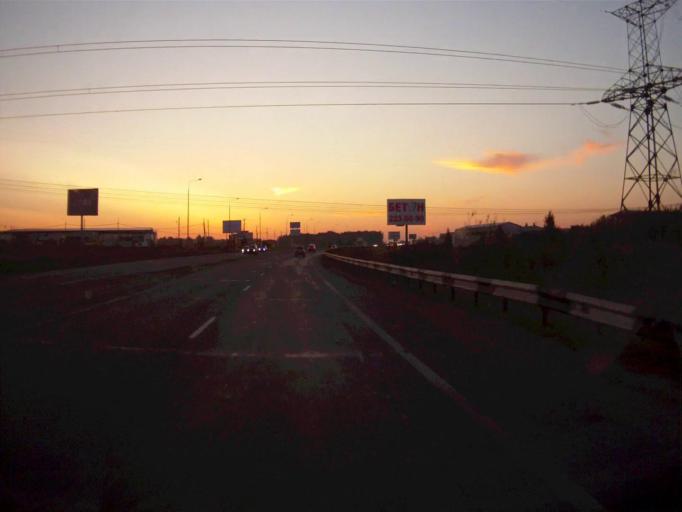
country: RU
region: Chelyabinsk
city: Roshchino
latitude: 55.1796
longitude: 61.2550
